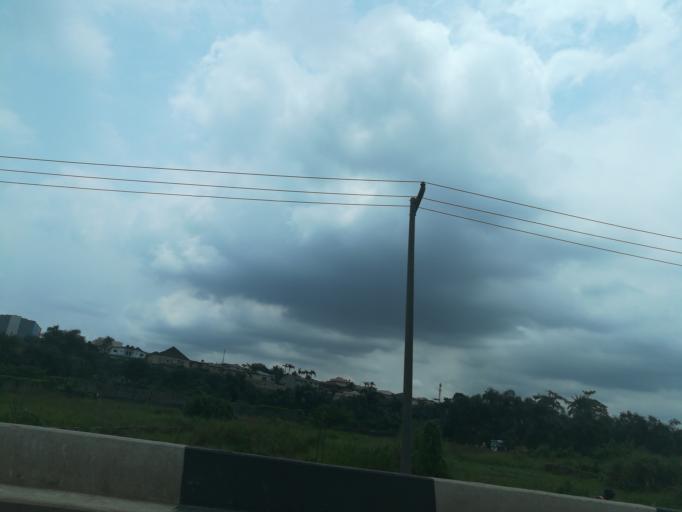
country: NG
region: Lagos
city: Ojota
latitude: 6.5795
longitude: 3.3945
